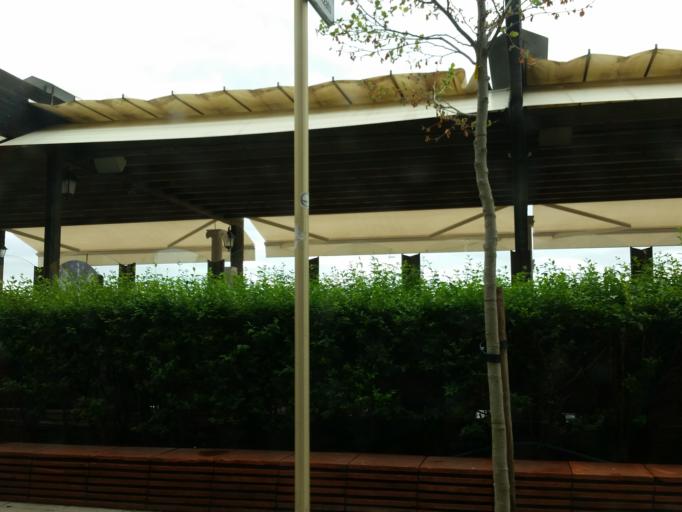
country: ES
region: Catalonia
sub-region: Provincia de Girona
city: Blanes
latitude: 41.6726
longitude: 2.7910
